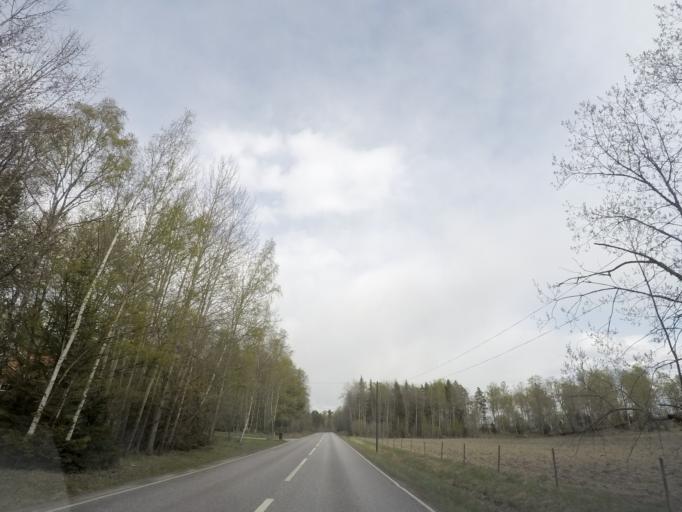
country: SE
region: Vaestmanland
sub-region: Kungsors Kommun
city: Kungsoer
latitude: 59.2851
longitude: 16.1460
